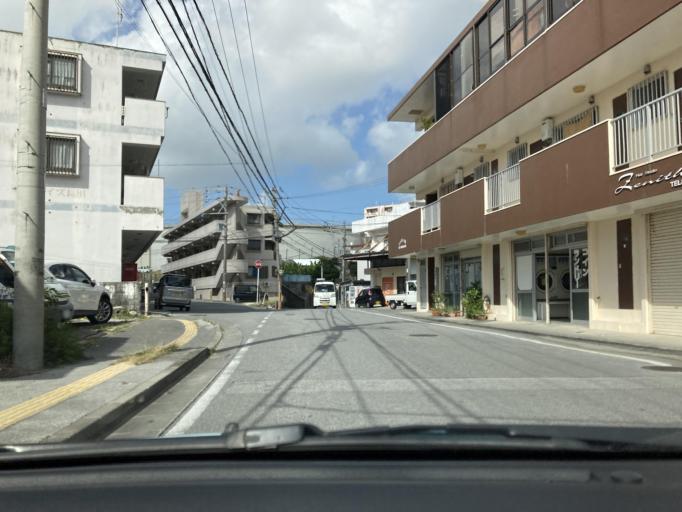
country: JP
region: Okinawa
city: Tomigusuku
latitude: 26.1991
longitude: 127.7037
